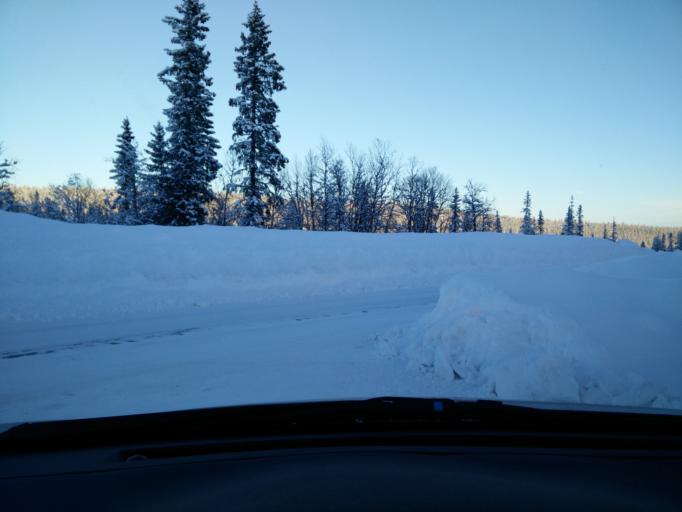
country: SE
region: Jaemtland
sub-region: Bergs Kommun
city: Hoverberg
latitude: 62.5003
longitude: 14.1089
